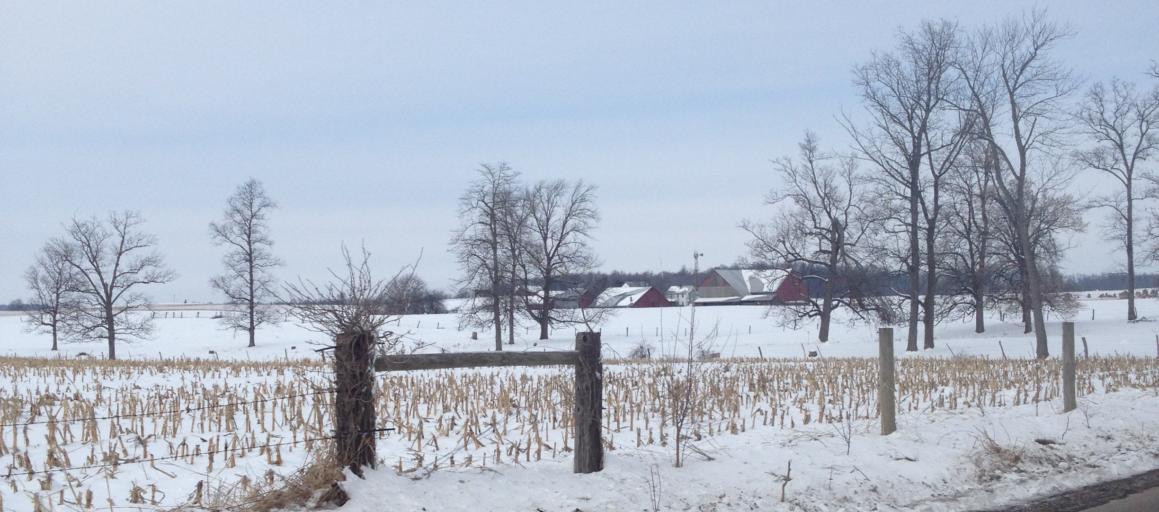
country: US
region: Ohio
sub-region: Wayne County
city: Apple Creek
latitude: 40.7039
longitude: -81.7461
